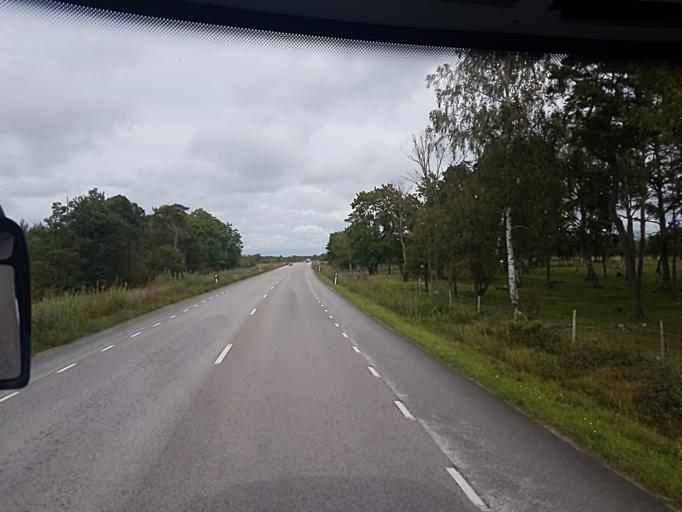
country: SE
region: Gotland
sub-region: Gotland
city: Vibble
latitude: 57.5190
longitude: 18.1623
